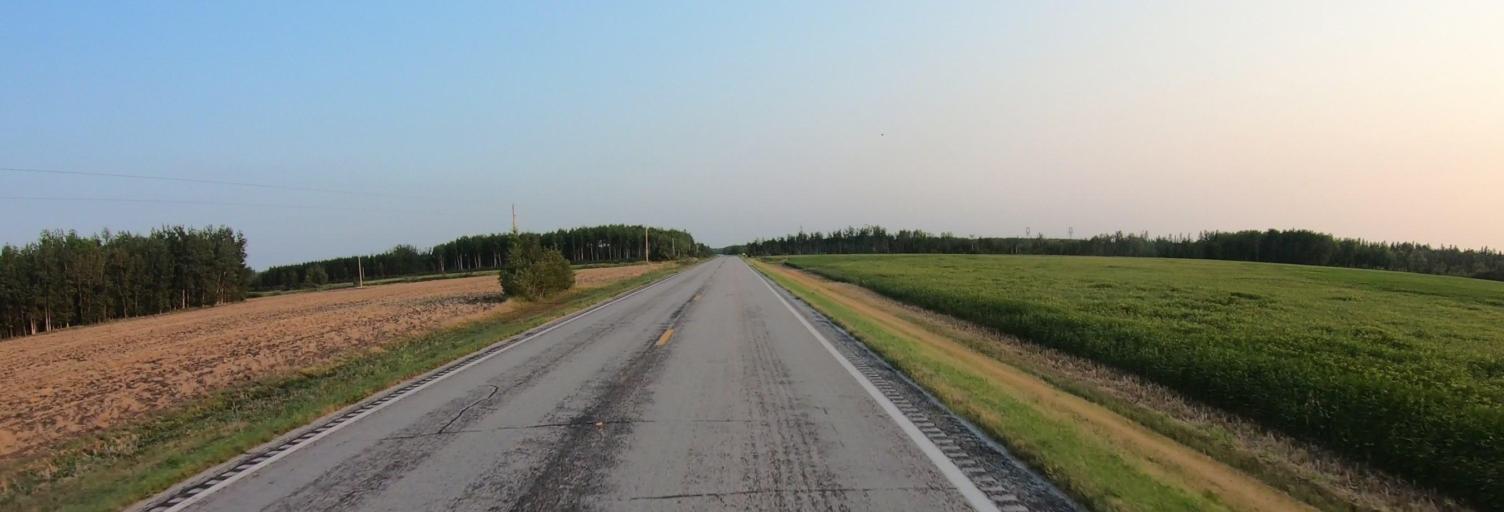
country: US
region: Minnesota
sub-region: Roseau County
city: Warroad
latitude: 48.7680
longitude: -95.3312
